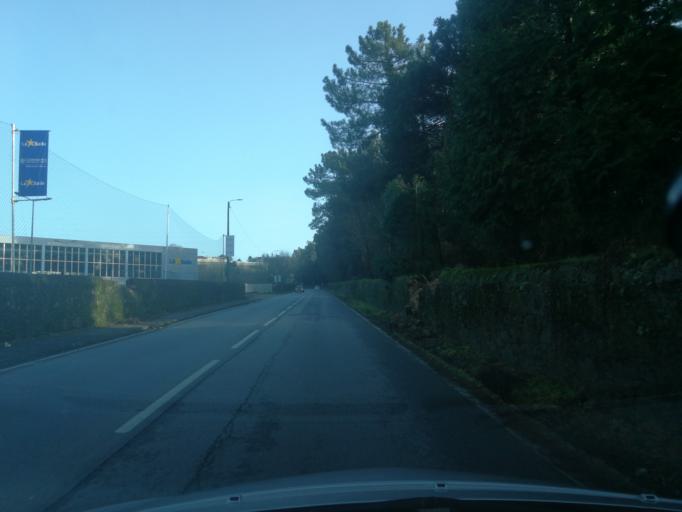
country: PT
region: Braga
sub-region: Barcelos
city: Barcelos
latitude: 41.5241
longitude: -8.6131
